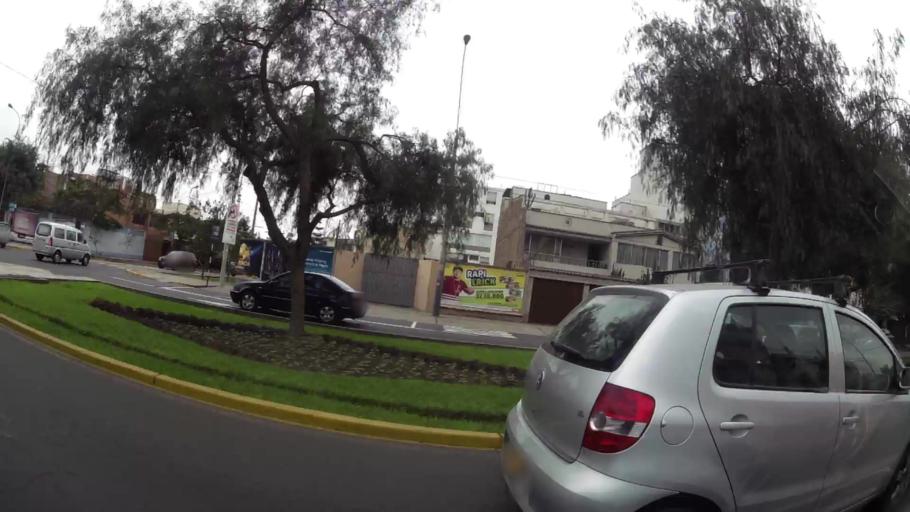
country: PE
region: Lima
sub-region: Lima
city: San Luis
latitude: -12.1040
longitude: -76.9937
